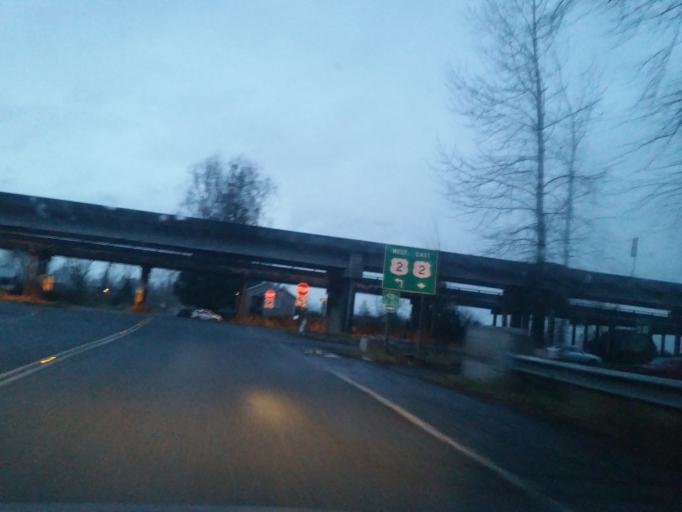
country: US
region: Washington
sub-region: Snohomish County
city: Everett
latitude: 47.9776
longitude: -122.1623
